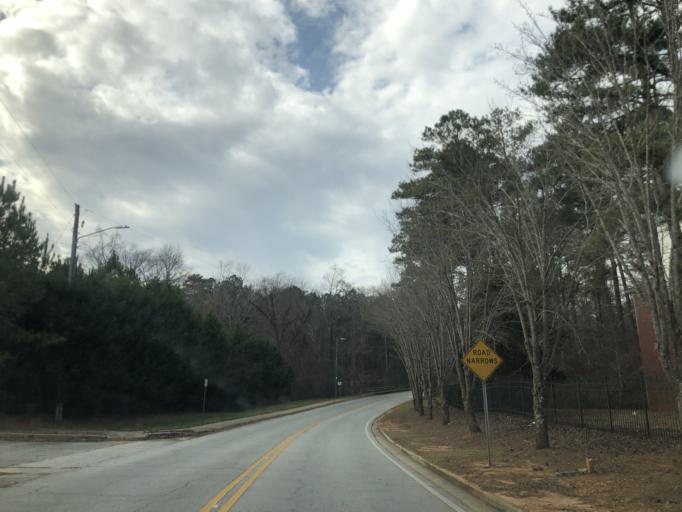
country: US
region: Georgia
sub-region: DeKalb County
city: Panthersville
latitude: 33.6655
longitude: -84.2099
